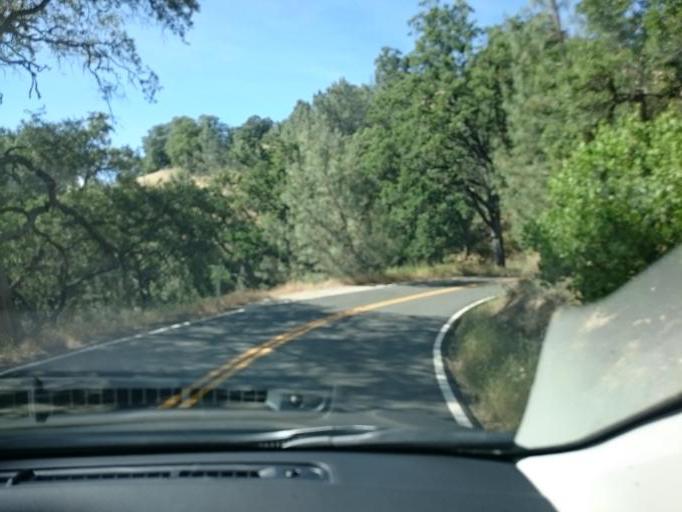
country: US
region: California
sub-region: Santa Clara County
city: East Foothills
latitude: 37.3374
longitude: -121.6537
